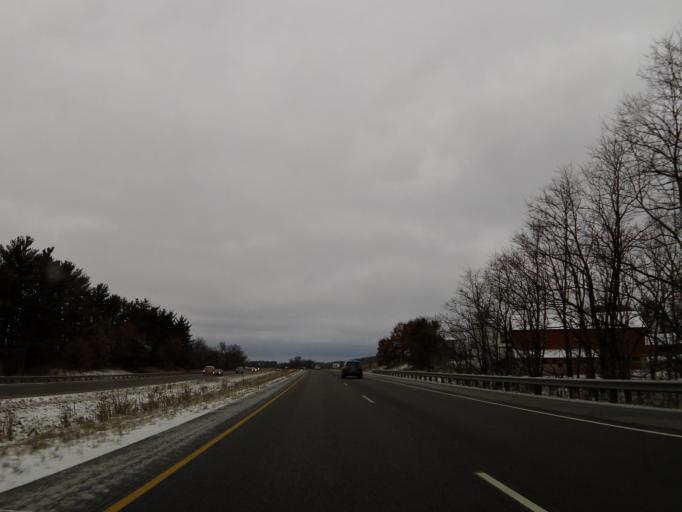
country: US
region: Wisconsin
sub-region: Eau Claire County
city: Fall Creek
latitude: 44.7202
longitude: -91.3517
